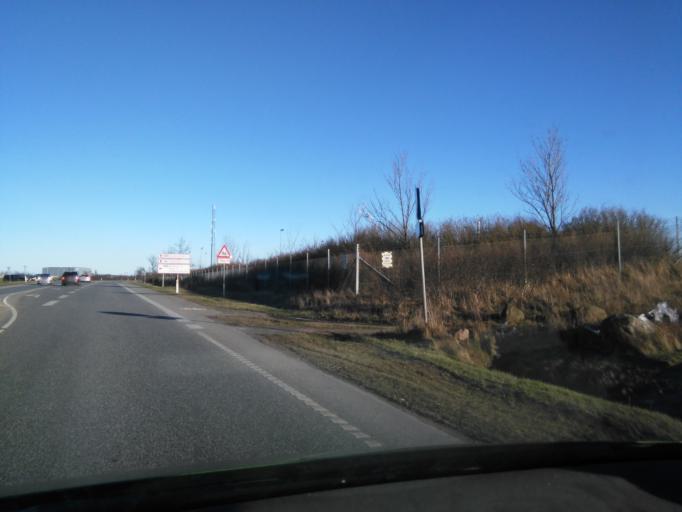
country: DK
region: North Denmark
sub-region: Mariagerfjord Kommune
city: Hobro
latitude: 56.6560
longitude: 9.7994
